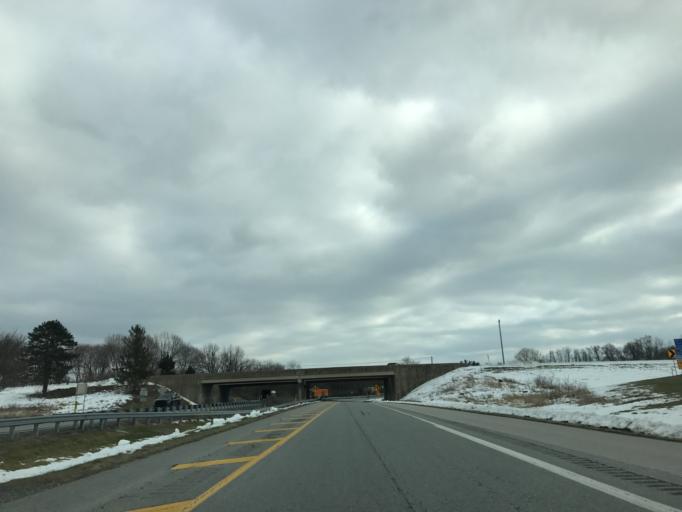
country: US
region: Pennsylvania
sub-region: York County
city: Shiloh
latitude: 39.9384
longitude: -76.7996
